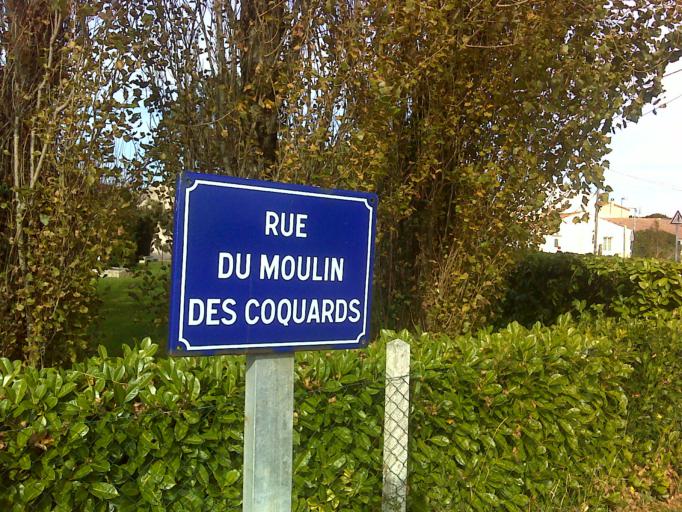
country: FR
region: Poitou-Charentes
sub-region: Departement de la Charente-Maritime
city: Marennes
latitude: 45.8313
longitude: -1.0973
